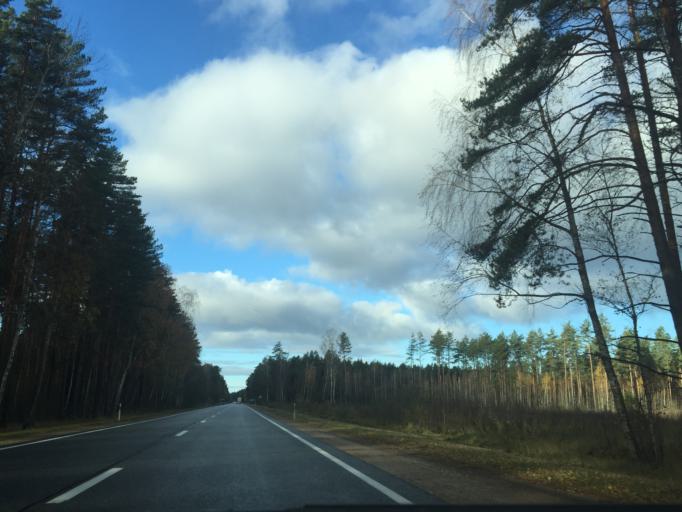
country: LV
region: Babite
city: Pinki
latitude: 56.9221
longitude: 23.9023
